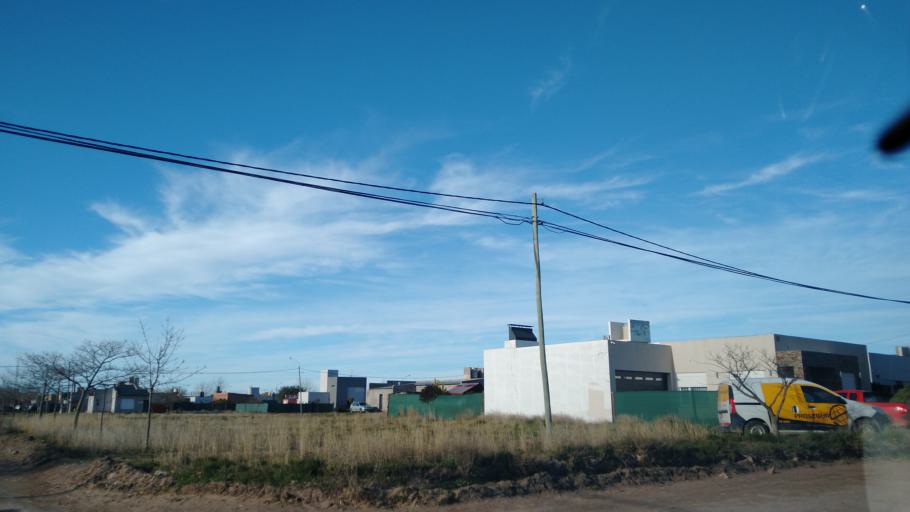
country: AR
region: Buenos Aires
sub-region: Partido de Bahia Blanca
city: Bahia Blanca
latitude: -38.7070
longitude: -62.2041
